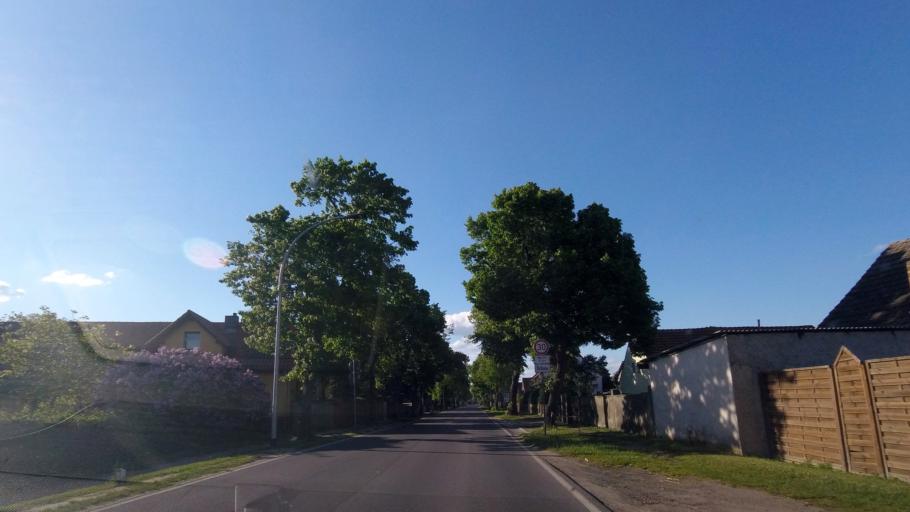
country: DE
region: Brandenburg
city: Luebben
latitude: 51.9292
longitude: 13.8943
